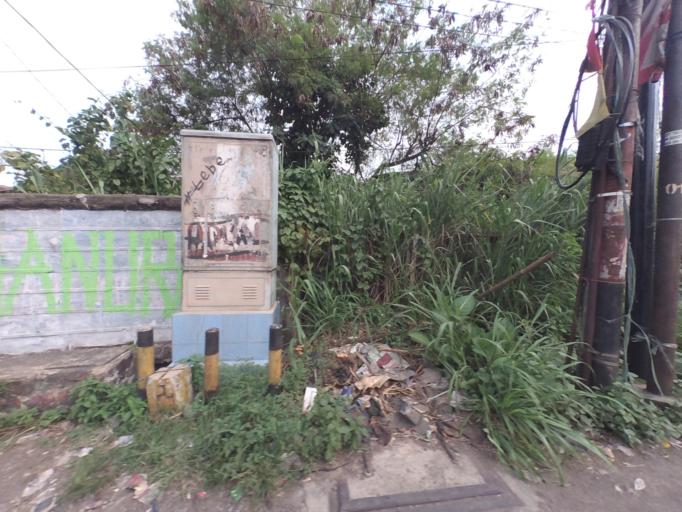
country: ID
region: West Java
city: Ciampea
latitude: -6.5549
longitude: 106.6963
